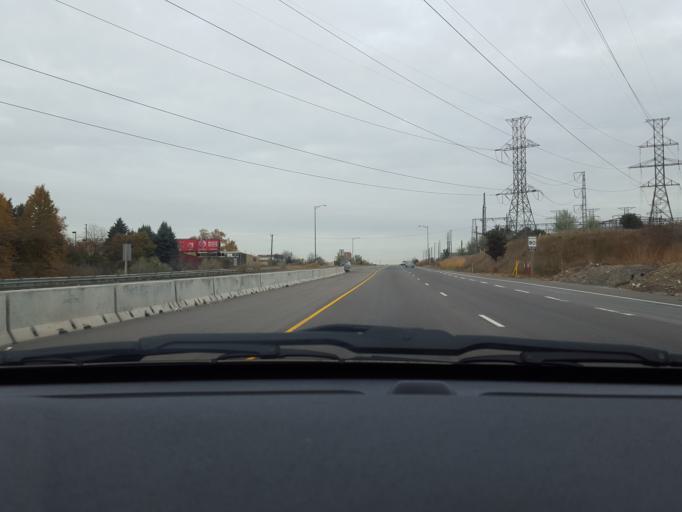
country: CA
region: Ontario
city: Etobicoke
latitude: 43.6803
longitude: -79.5790
